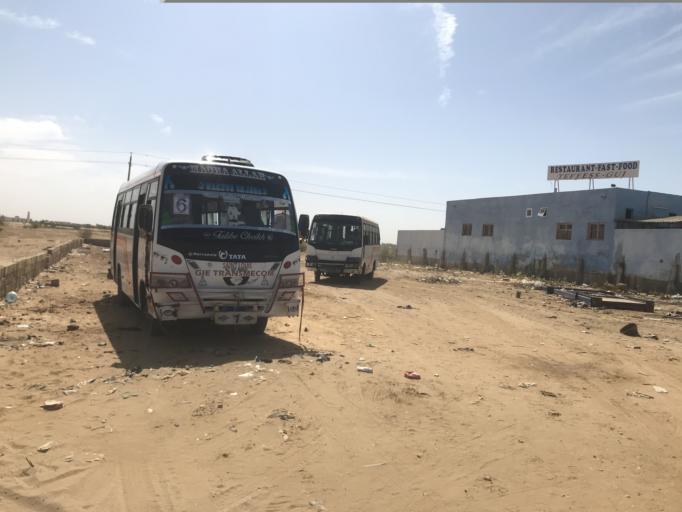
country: SN
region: Saint-Louis
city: Saint-Louis
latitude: 16.0601
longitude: -16.4162
